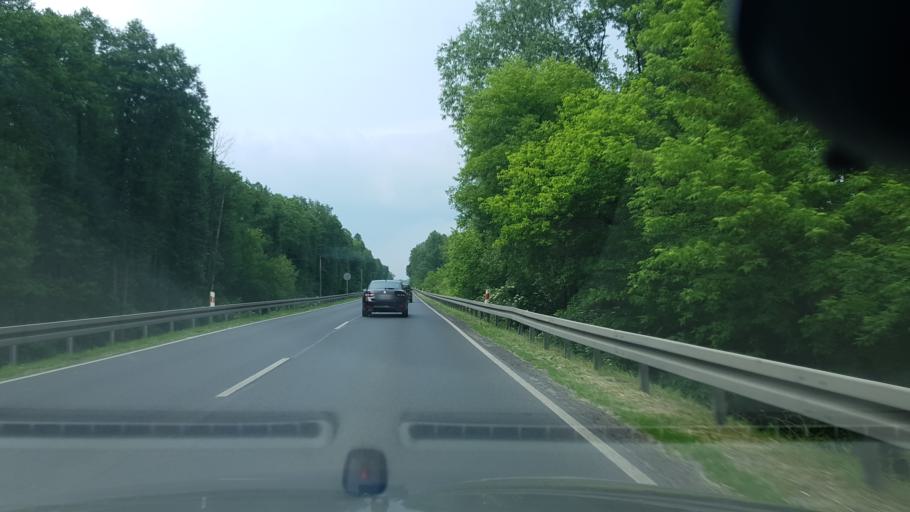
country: PL
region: Masovian Voivodeship
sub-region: Powiat legionowski
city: Wieliszew
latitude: 52.4366
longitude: 20.9909
